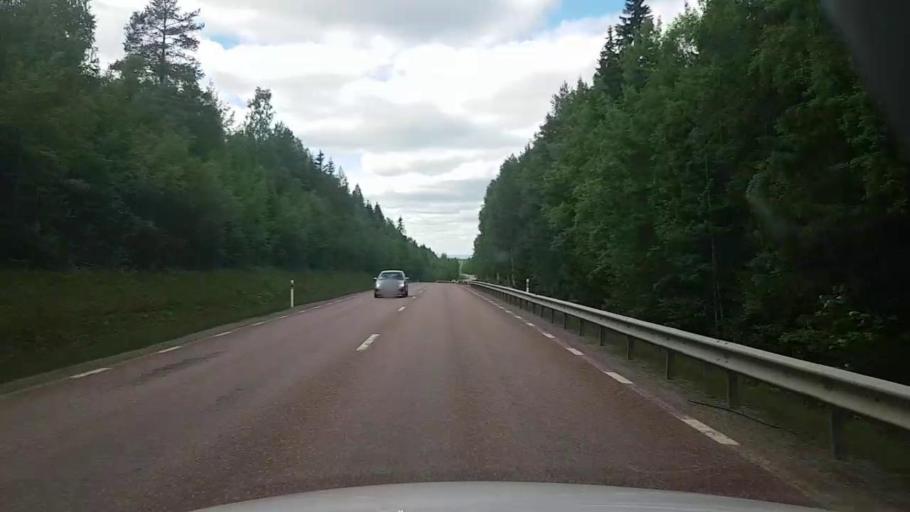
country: SE
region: Gaevleborg
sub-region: Ljusdals Kommun
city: Ljusdal
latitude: 61.7995
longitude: 16.1175
